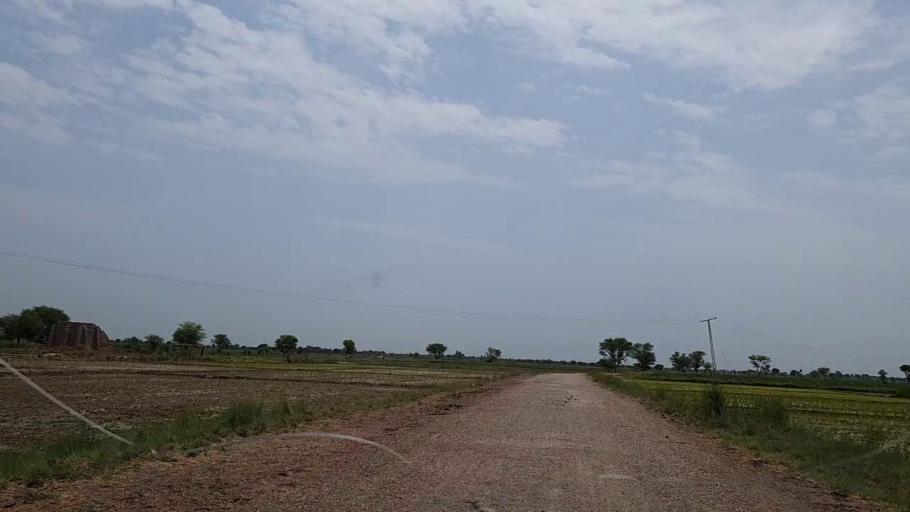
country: PK
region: Sindh
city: Tharu Shah
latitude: 26.9182
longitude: 68.0813
